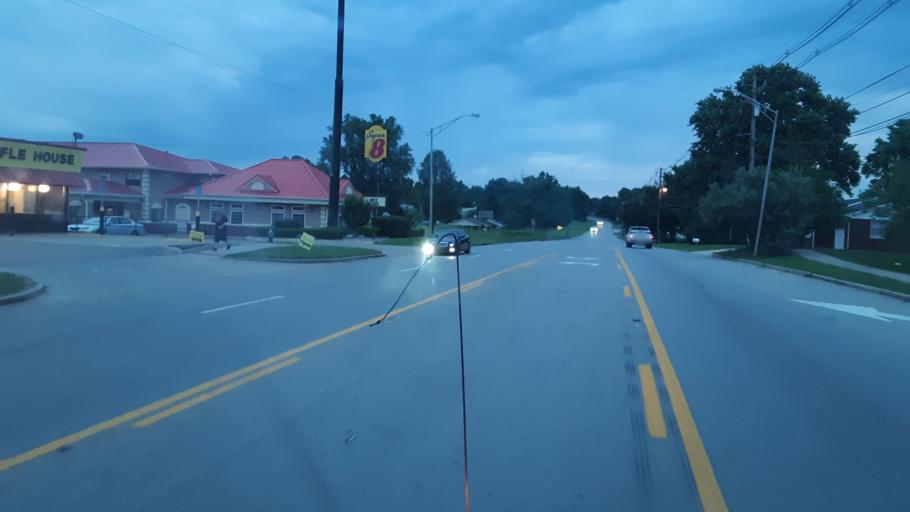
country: US
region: Kentucky
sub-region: Hardin County
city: Elizabethtown
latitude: 37.7158
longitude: -85.8247
